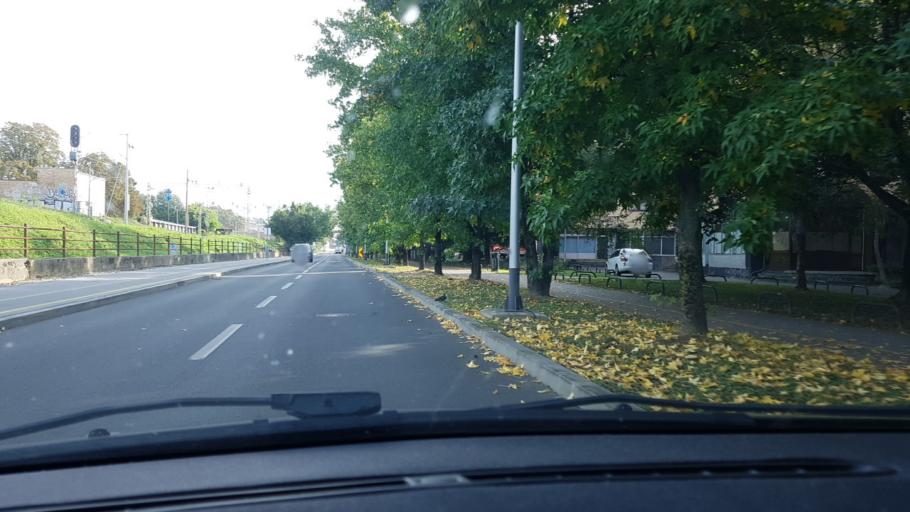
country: HR
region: Grad Zagreb
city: Zagreb - Centar
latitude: 45.8028
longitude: 15.9671
